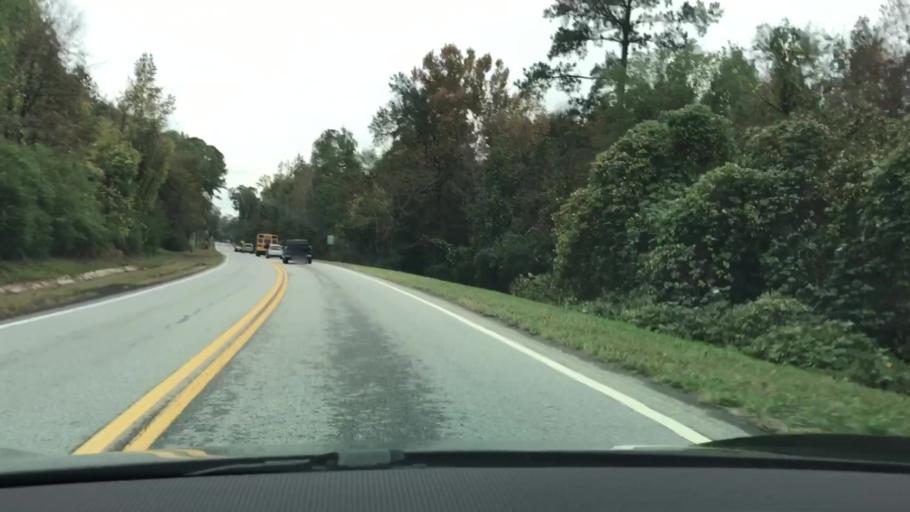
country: US
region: Georgia
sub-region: Greene County
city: Greensboro
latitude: 33.5859
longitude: -83.1927
